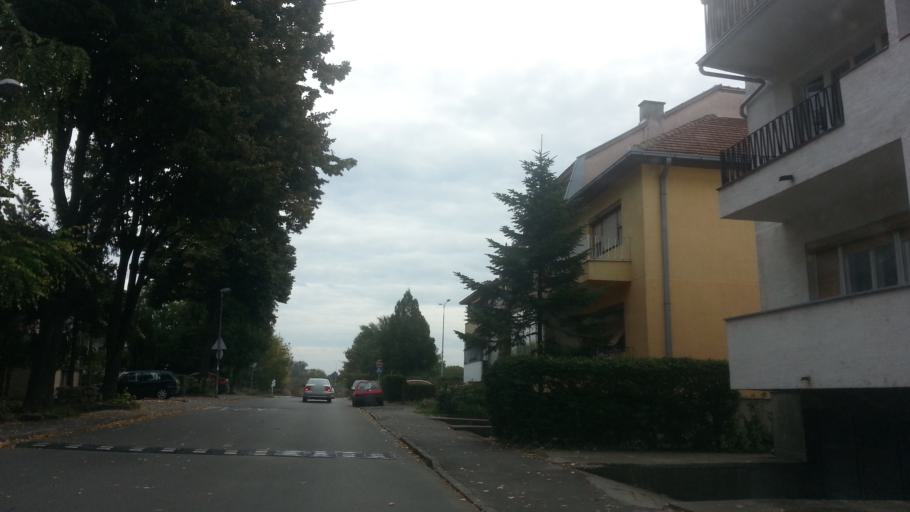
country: RS
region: Central Serbia
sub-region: Belgrade
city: Zemun
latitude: 44.8560
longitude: 20.3701
